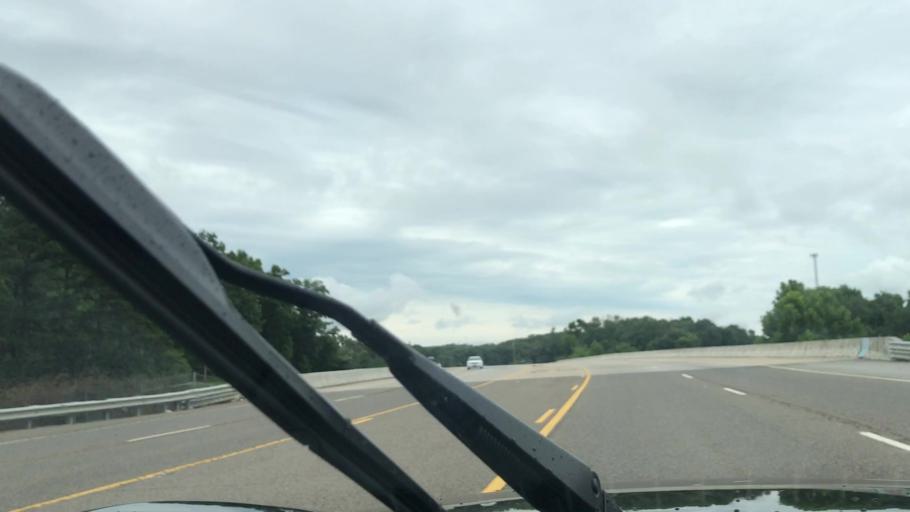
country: US
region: Tennessee
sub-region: Scott County
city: Oneida
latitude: 36.4762
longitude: -84.5395
